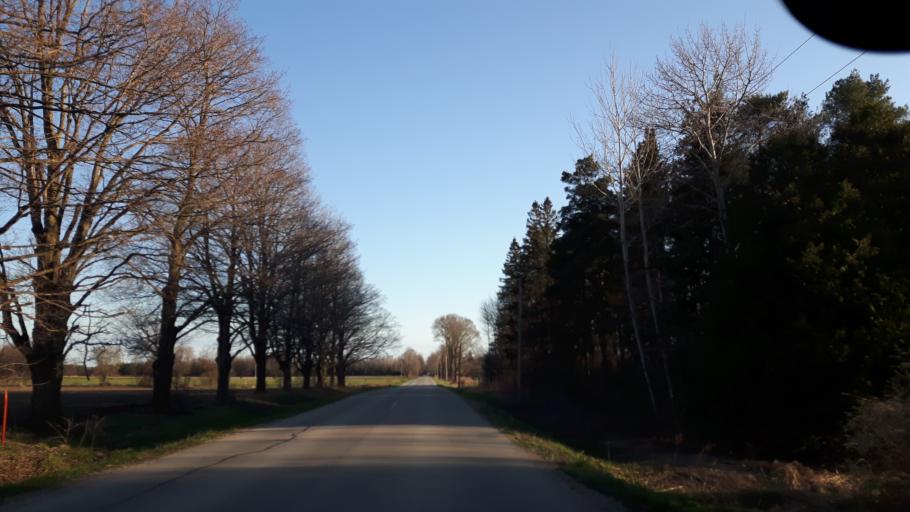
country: CA
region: Ontario
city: Goderich
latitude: 43.6330
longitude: -81.6847
